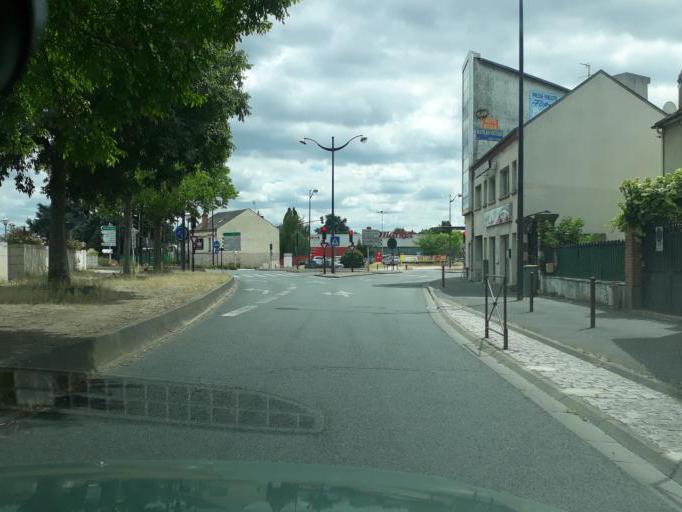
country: FR
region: Centre
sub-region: Departement du Loiret
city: Orleans
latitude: 47.8890
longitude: 1.8948
